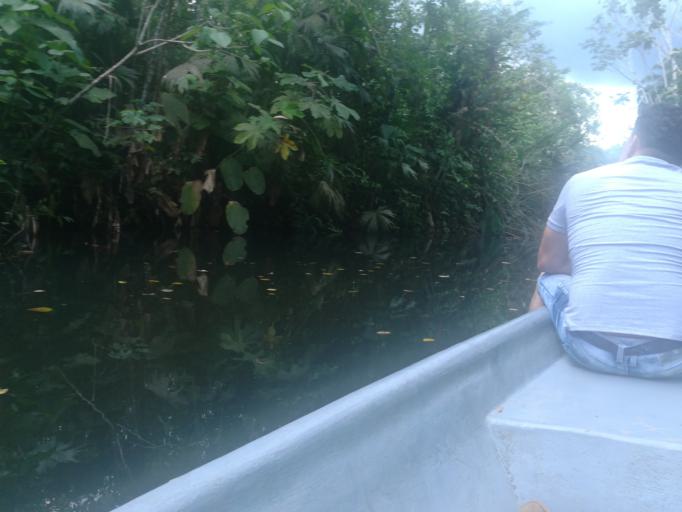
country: EC
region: Napo
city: Tena
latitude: -1.0396
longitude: -77.6651
